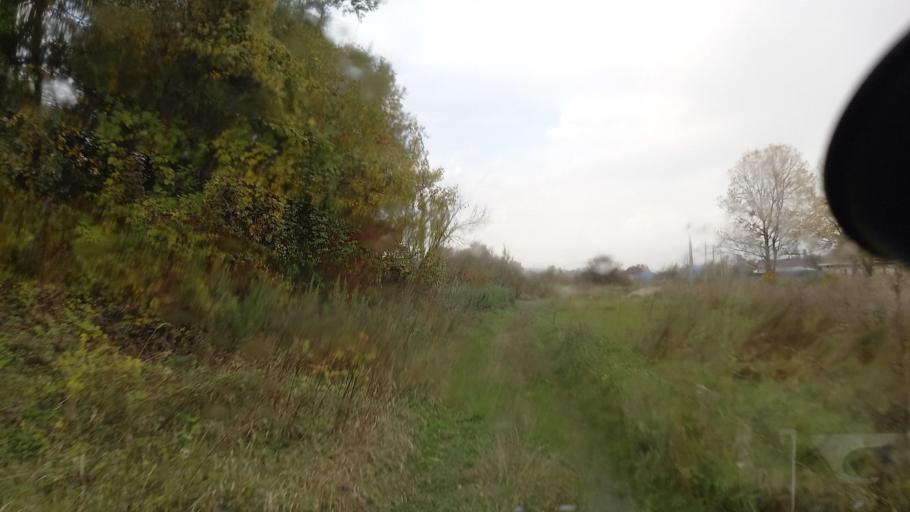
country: RU
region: Krasnodarskiy
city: Shedok
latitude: 44.1732
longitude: 40.8434
